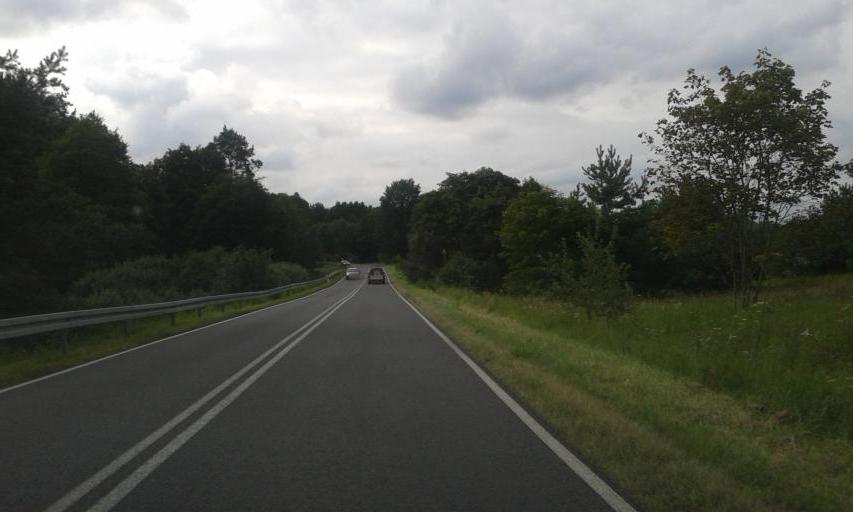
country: PL
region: West Pomeranian Voivodeship
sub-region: Powiat szczecinecki
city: Borne Sulinowo
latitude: 53.7183
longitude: 16.5534
